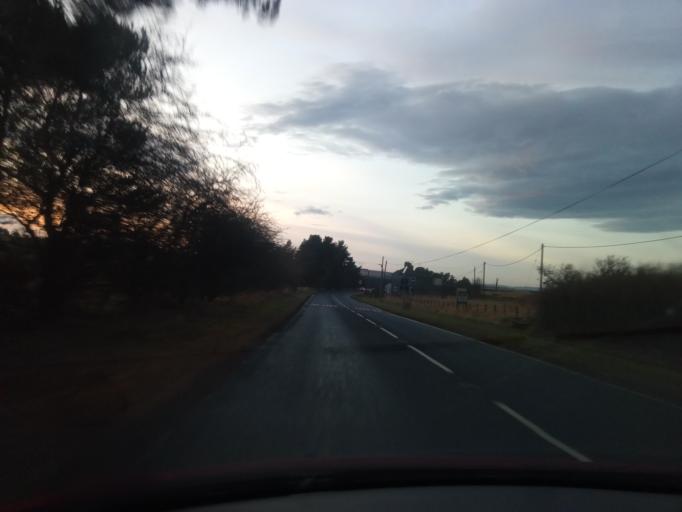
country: GB
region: England
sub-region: Northumberland
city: Otterburn
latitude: 55.2324
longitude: -2.1856
